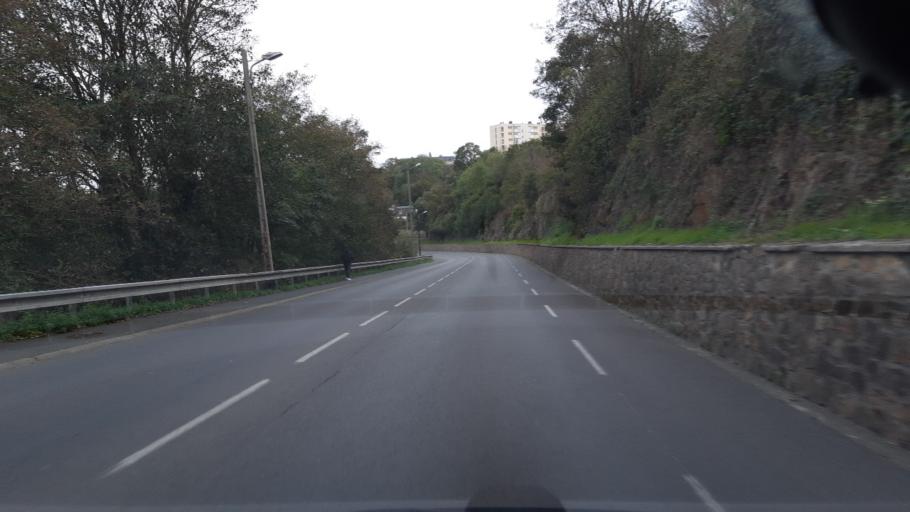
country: FR
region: Lower Normandy
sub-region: Departement de la Manche
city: Donville-les-Bains
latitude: 48.8437
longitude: -1.5838
